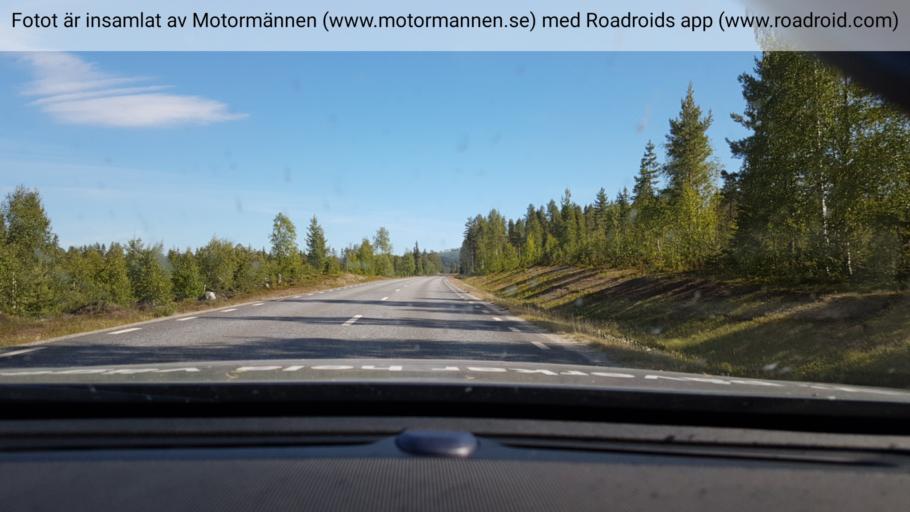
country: SE
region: Vaesterbotten
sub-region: Lycksele Kommun
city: Soderfors
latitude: 64.7379
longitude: 18.2050
